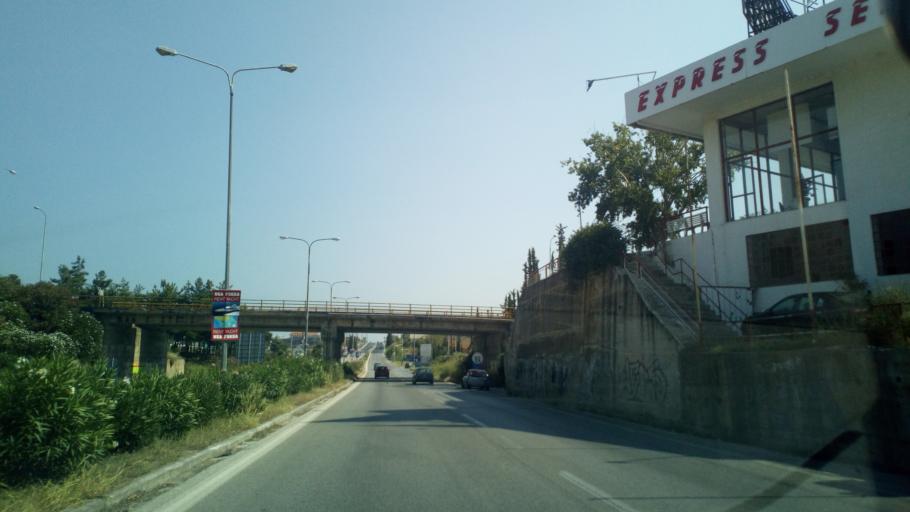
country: GR
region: Central Macedonia
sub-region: Nomos Chalkidikis
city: Nea Moudhania
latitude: 40.2431
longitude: 23.2986
